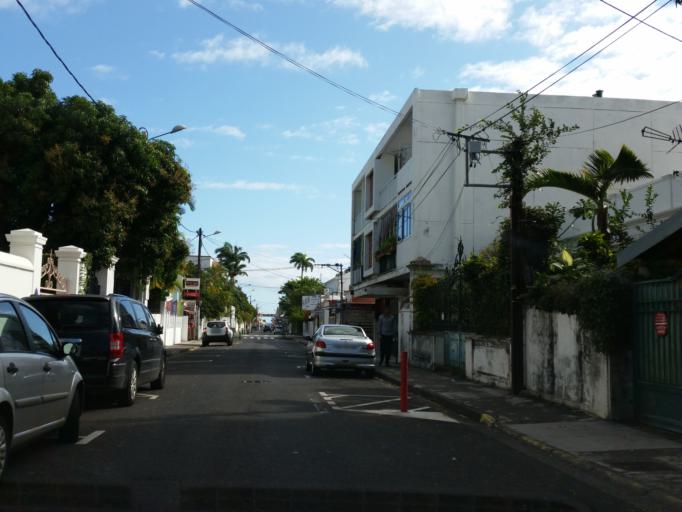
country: RE
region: Reunion
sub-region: Reunion
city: Saint-Denis
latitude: -20.8843
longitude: 55.4520
